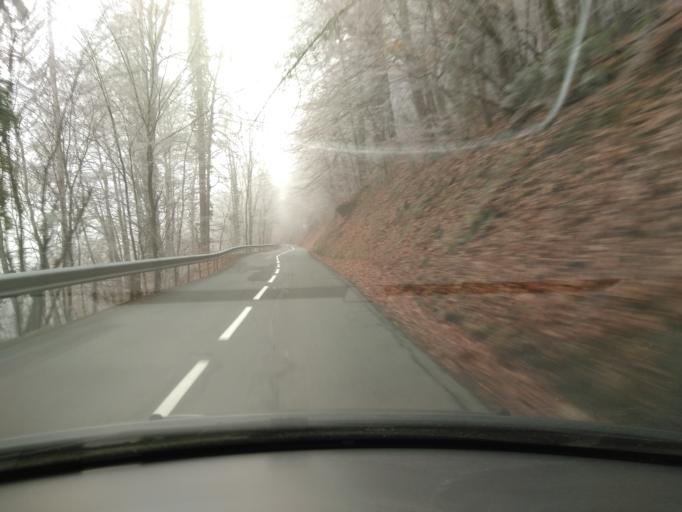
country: FR
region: Rhone-Alpes
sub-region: Departement de la Haute-Savoie
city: Sallanches
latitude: 45.9489
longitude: 6.6242
